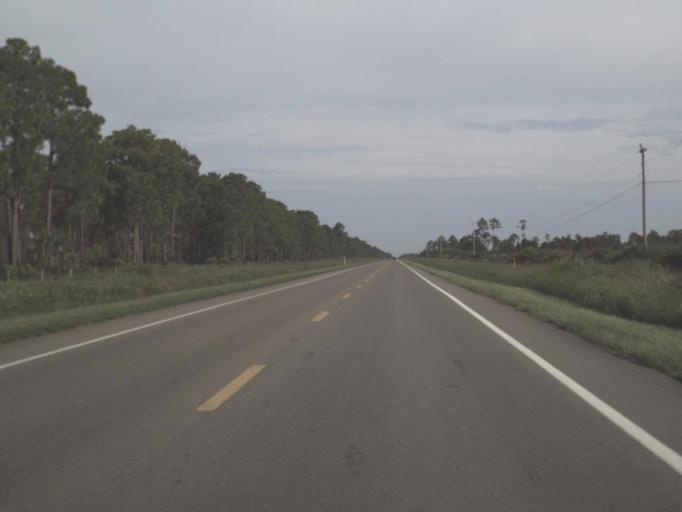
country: US
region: Florida
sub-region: Lee County
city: Olga
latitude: 26.8614
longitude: -81.7597
